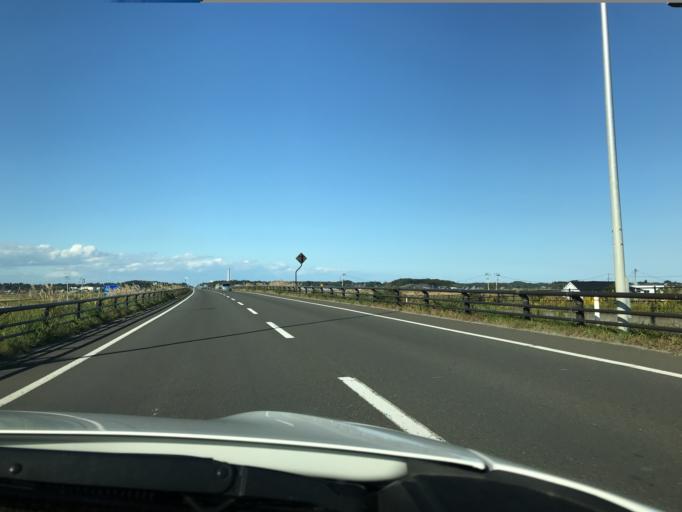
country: JP
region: Miyagi
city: Marumori
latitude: 37.7888
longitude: 140.9440
